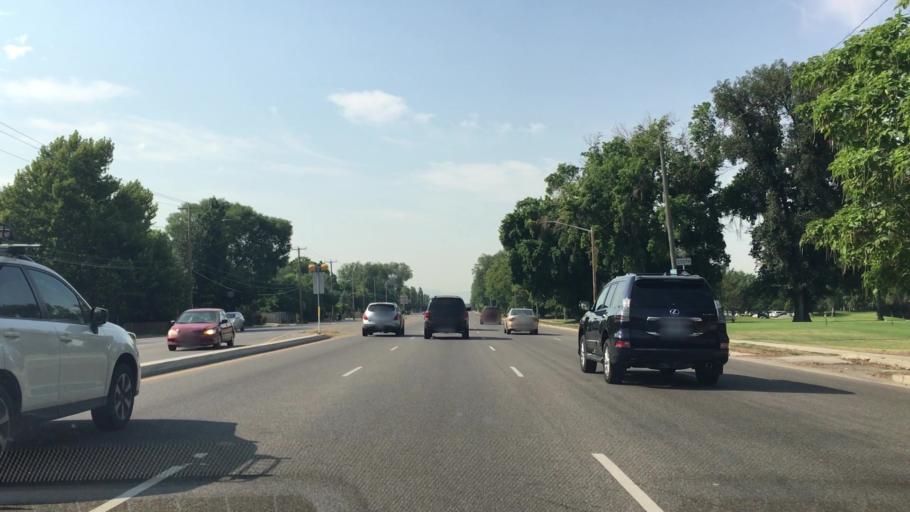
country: US
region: Utah
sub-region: Salt Lake County
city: South Salt Lake
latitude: 40.7123
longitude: -111.8714
